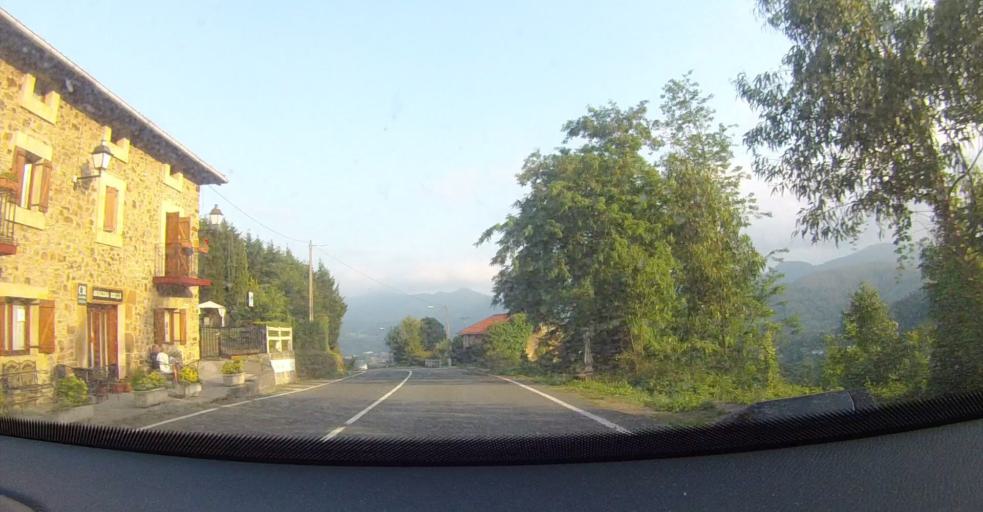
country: ES
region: Basque Country
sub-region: Bizkaia
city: Sopuerta
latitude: 43.2906
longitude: -3.1642
